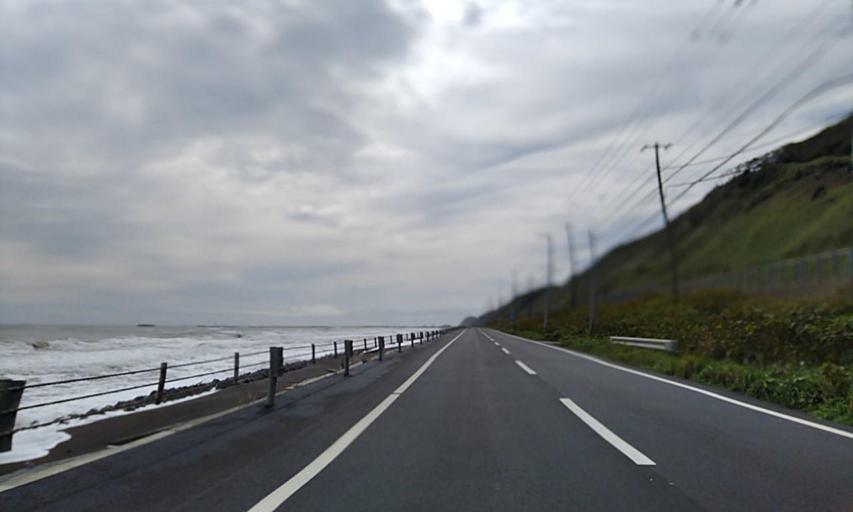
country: JP
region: Hokkaido
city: Kushiro
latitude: 42.8182
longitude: 143.8342
